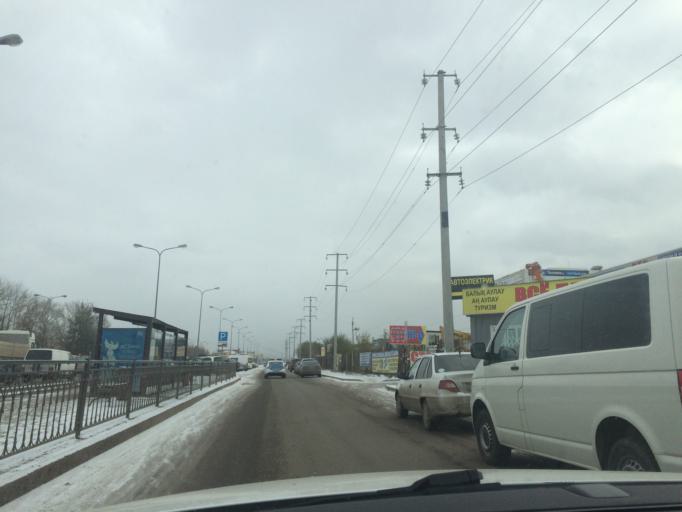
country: KZ
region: Astana Qalasy
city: Astana
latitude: 51.1800
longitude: 71.4642
